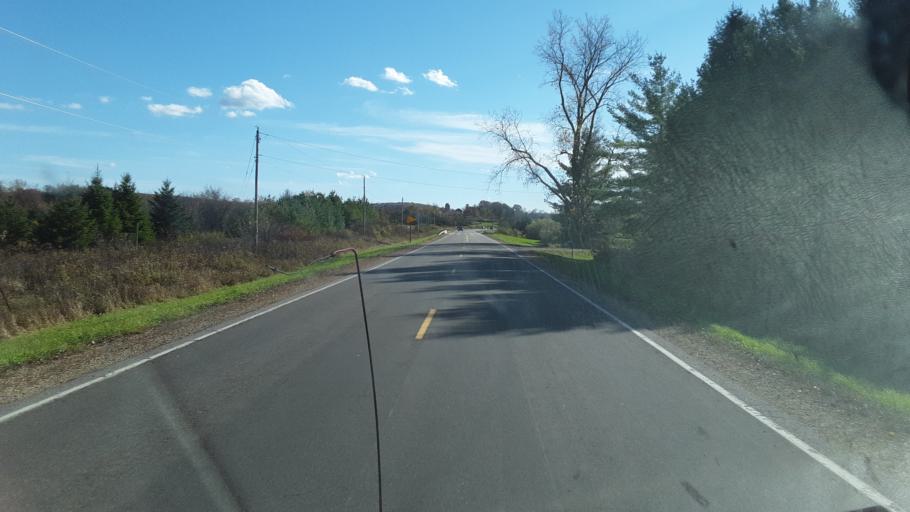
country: US
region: Wisconsin
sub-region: Sauk County
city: Reedsburg
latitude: 43.5658
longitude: -90.1331
